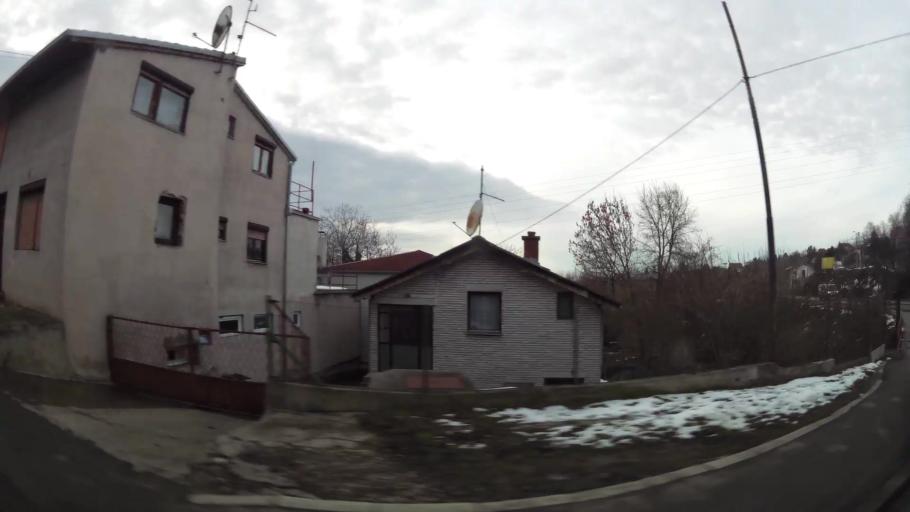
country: RS
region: Central Serbia
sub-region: Belgrade
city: Vozdovac
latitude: 44.7394
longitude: 20.4867
